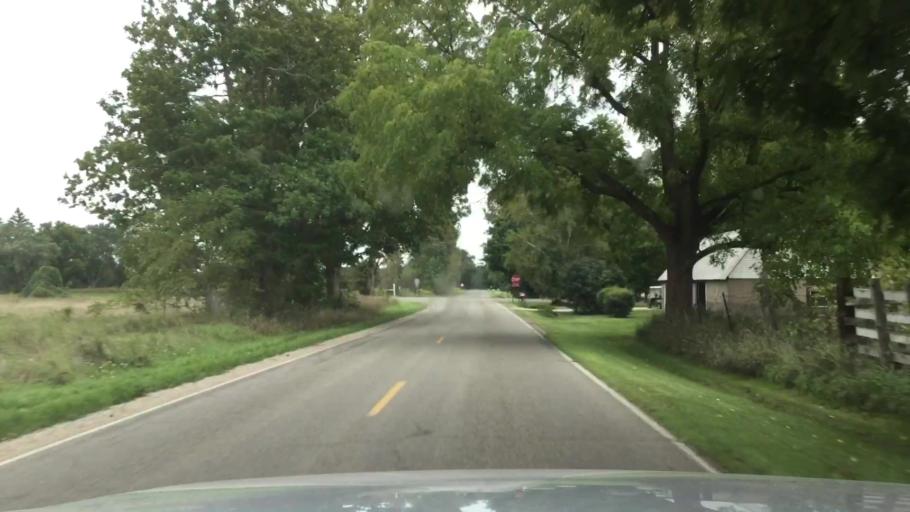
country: US
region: Michigan
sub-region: Shiawassee County
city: Durand
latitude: 42.8236
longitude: -84.0105
